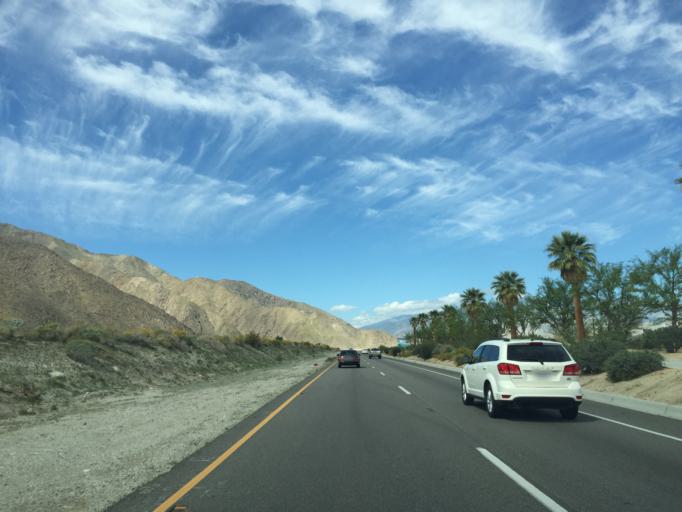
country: US
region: California
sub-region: Riverside County
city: Palm Springs
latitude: 33.8644
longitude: -116.5670
